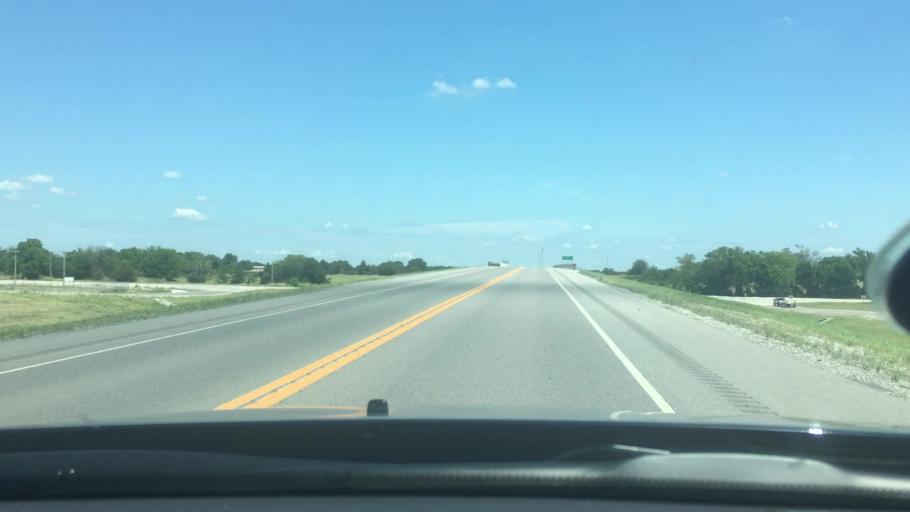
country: US
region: Oklahoma
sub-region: Bryan County
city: Durant
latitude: 33.9843
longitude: -96.3396
